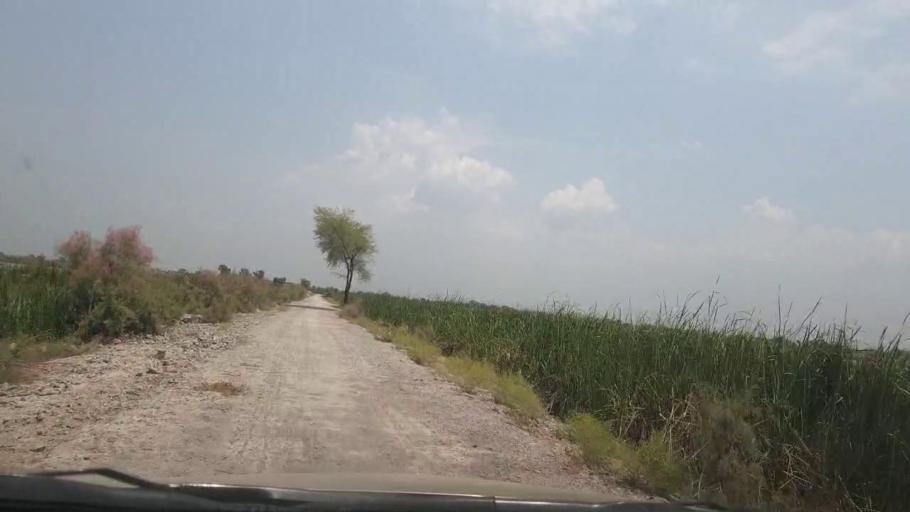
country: PK
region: Sindh
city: Naudero
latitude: 27.7223
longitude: 68.3265
